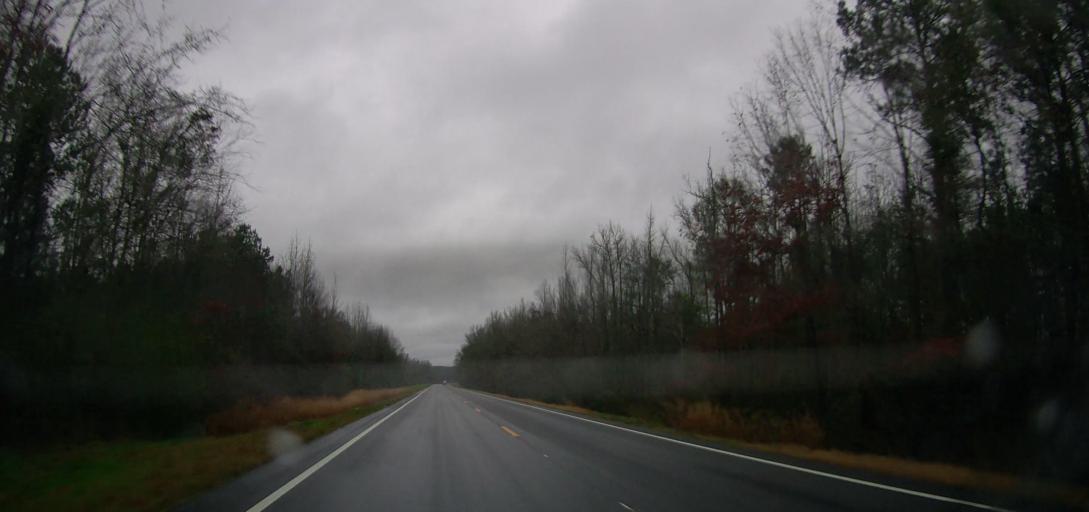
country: US
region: Alabama
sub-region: Chilton County
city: Thorsby
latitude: 32.7604
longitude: -86.8743
